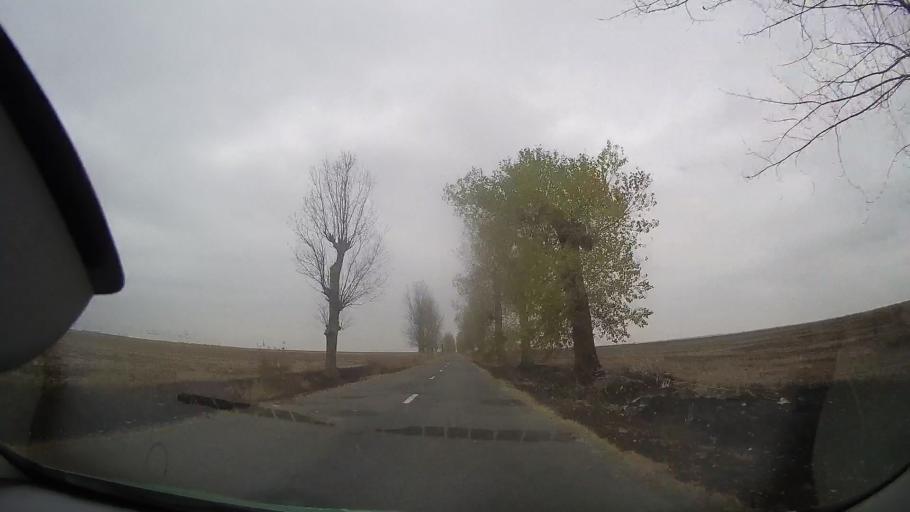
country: RO
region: Ialomita
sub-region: Comuna Grindu
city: Grindu
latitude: 44.7715
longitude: 26.8852
